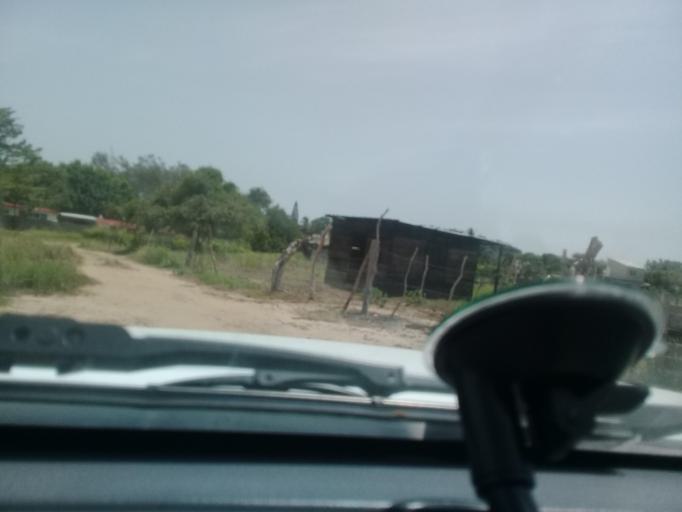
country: MX
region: Veracruz
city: Anahuac
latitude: 22.2276
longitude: -97.8262
